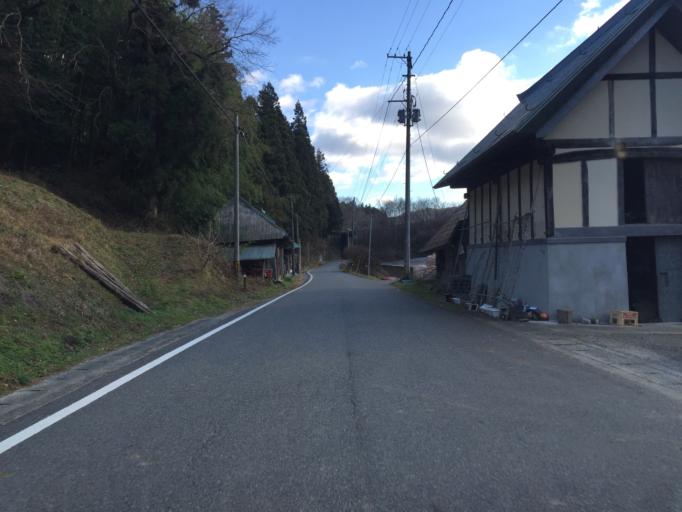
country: JP
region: Fukushima
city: Funehikimachi-funehiki
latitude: 37.2306
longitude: 140.7051
